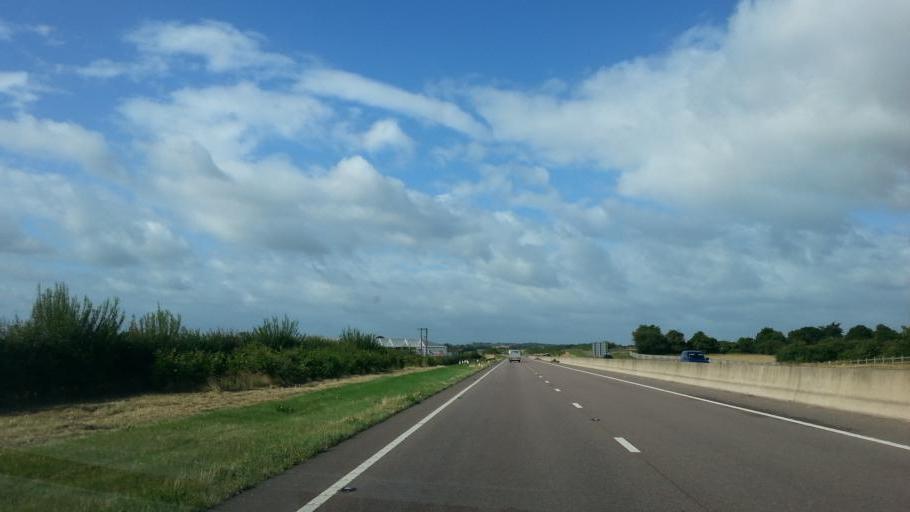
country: GB
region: England
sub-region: Nottinghamshire
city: East Bridgford
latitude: 52.9768
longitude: -0.9515
